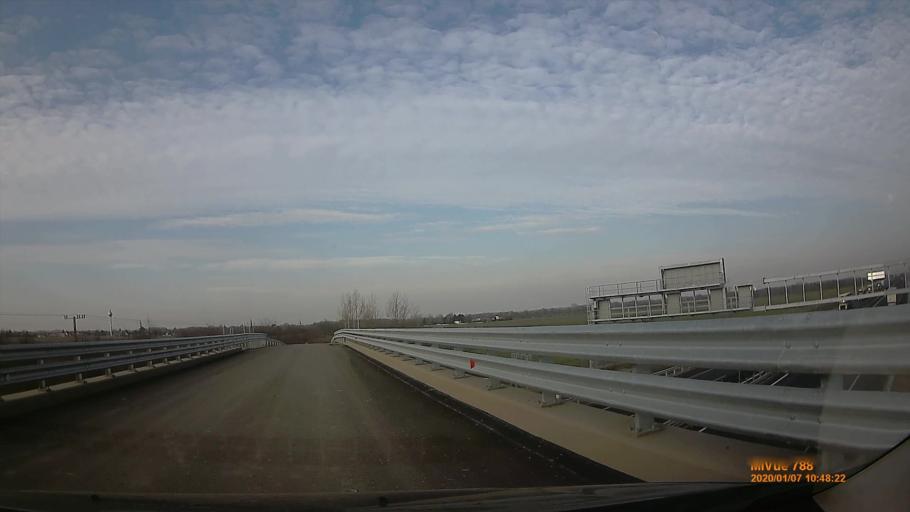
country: HU
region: Gyor-Moson-Sopron
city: Rajka
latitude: 47.9143
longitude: 17.1807
